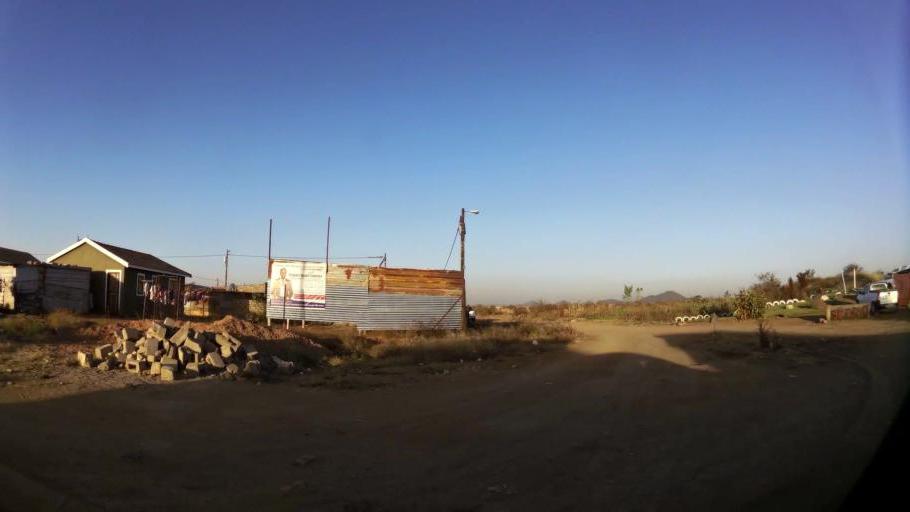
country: ZA
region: North-West
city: Ga-Rankuwa
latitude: -25.6013
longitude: 28.0919
